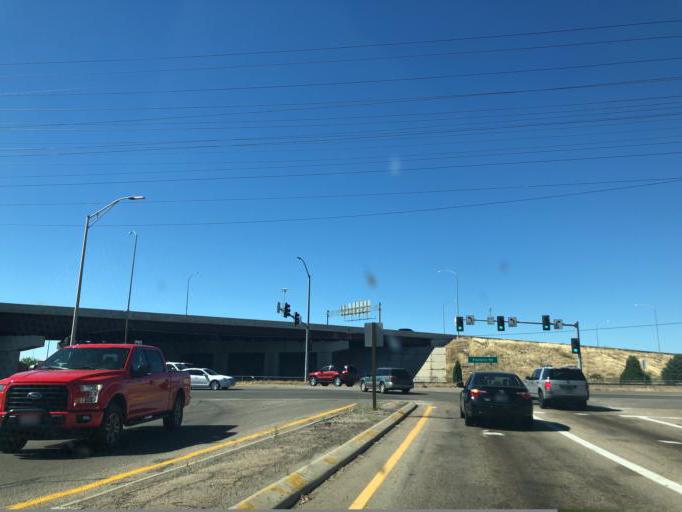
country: US
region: Idaho
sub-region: Ada County
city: Garden City
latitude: 43.6044
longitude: -116.2770
